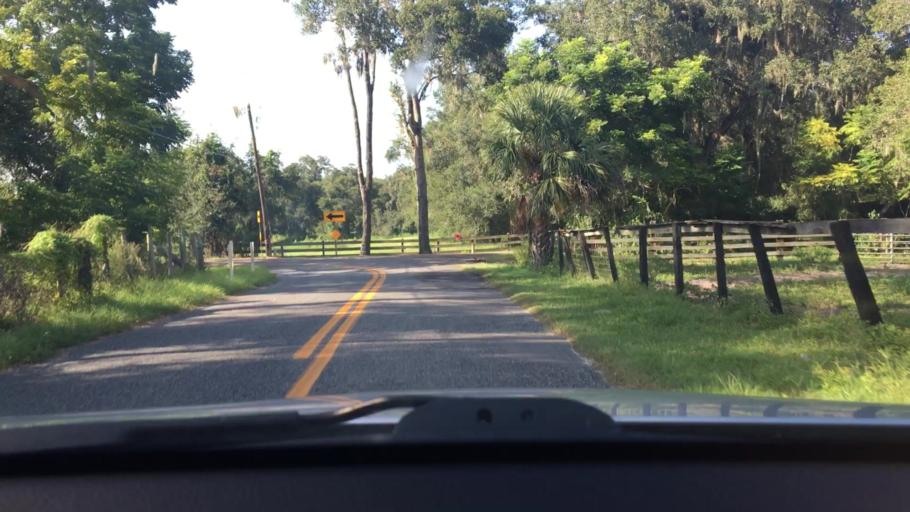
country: US
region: Florida
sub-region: Volusia County
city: Lake Helen
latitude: 28.9701
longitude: -81.2151
